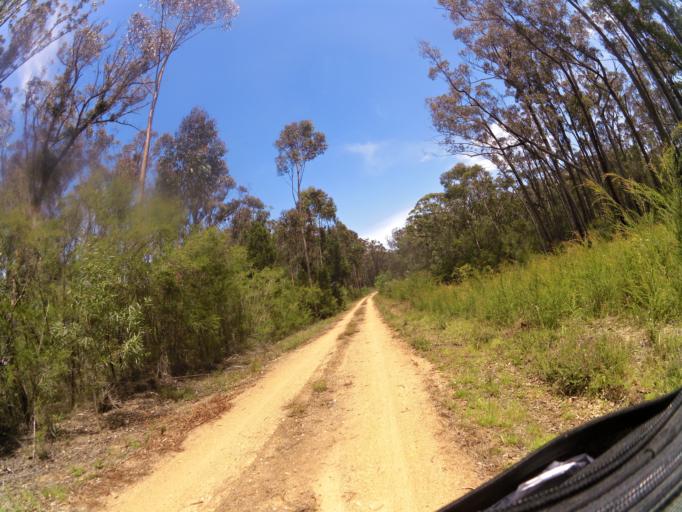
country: AU
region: Victoria
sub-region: East Gippsland
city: Lakes Entrance
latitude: -37.7539
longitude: 147.9709
